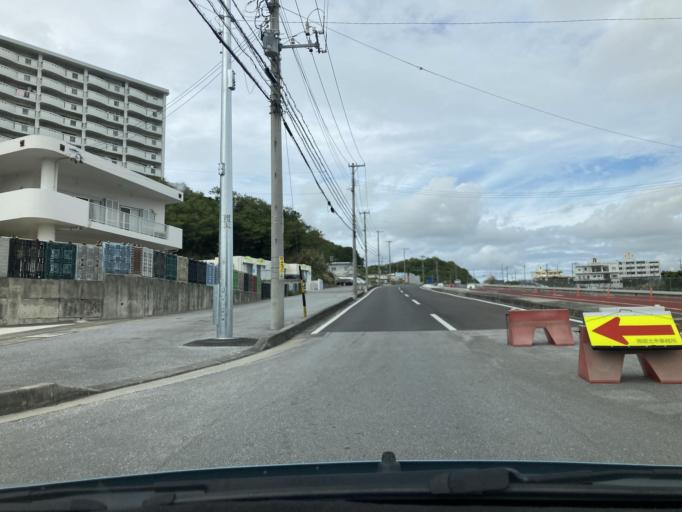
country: JP
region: Okinawa
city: Tomigusuku
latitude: 26.1661
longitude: 127.6781
